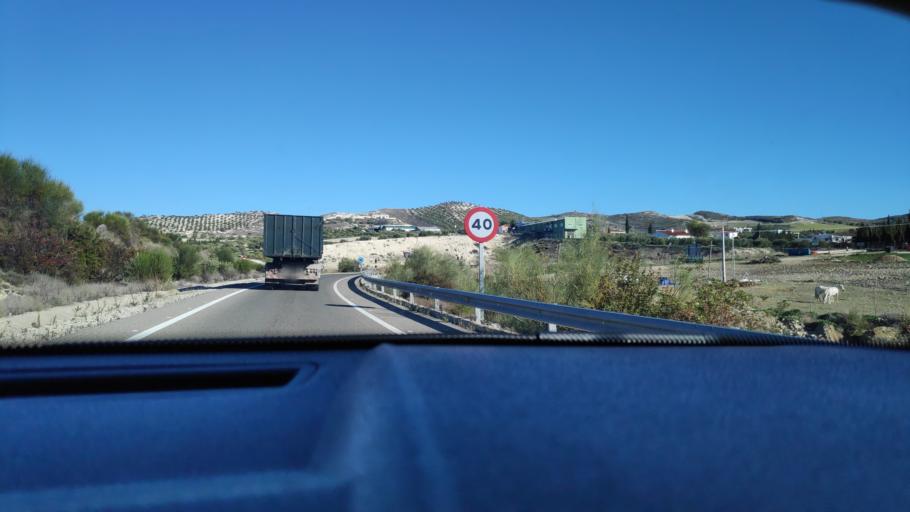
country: ES
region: Andalusia
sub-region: Province of Cordoba
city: Baena
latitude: 37.6222
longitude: -4.3005
